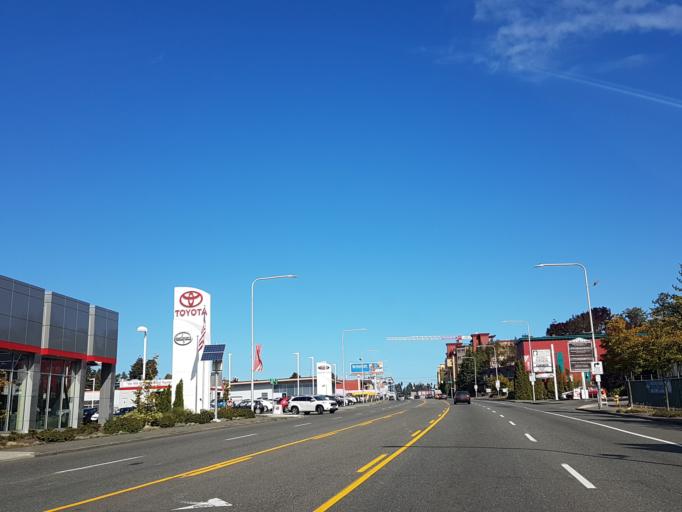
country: US
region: Washington
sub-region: King County
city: Lake Forest Park
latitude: 47.7258
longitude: -122.2923
